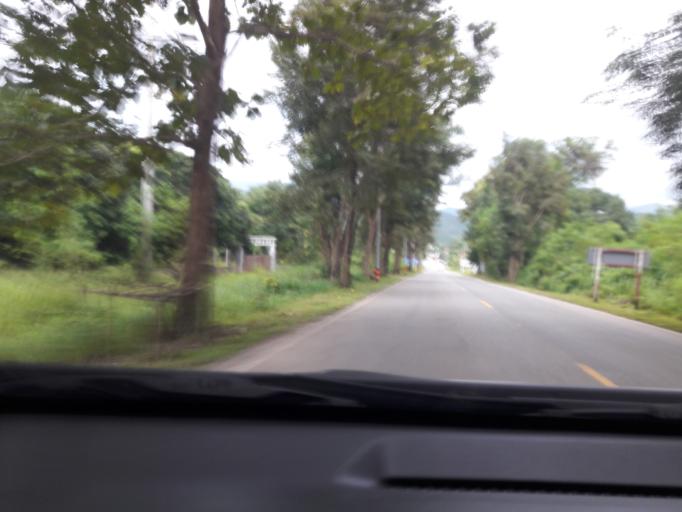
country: TH
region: Mae Hong Son
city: Mae Hi
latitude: 19.3026
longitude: 98.4619
